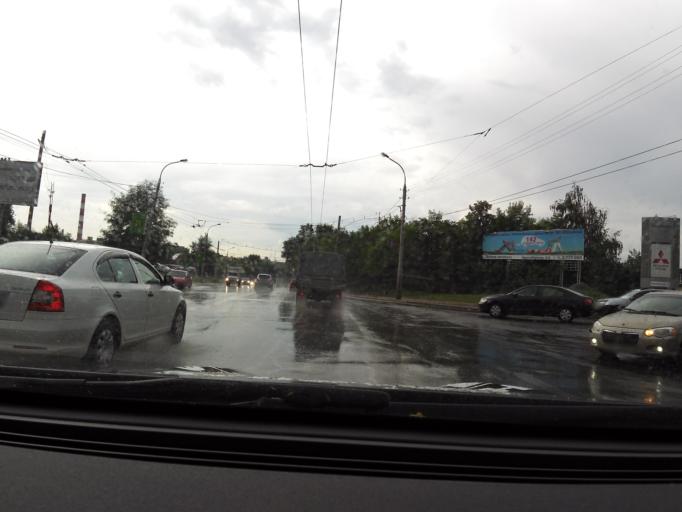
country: RU
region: Bashkortostan
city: Ufa
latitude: 54.7504
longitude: 55.9801
